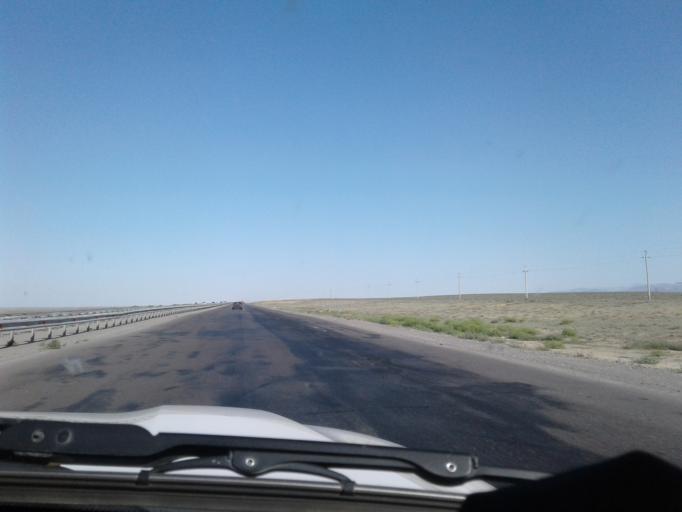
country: TM
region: Ahal
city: Kaka
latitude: 37.3423
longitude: 59.6905
